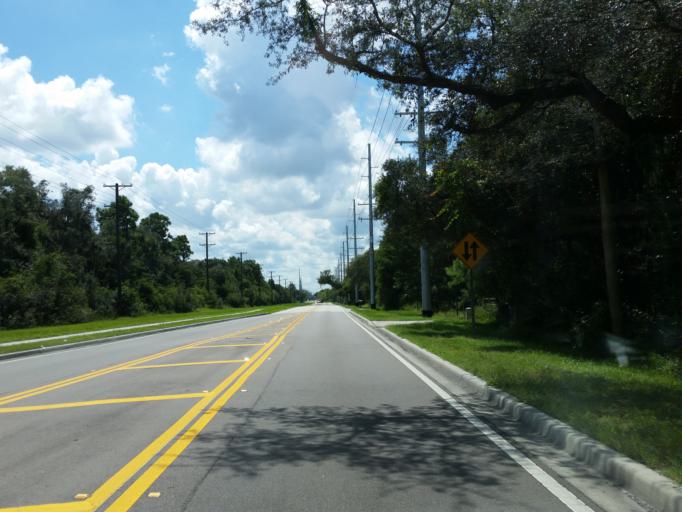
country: US
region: Florida
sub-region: Hillsborough County
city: Riverview
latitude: 27.8508
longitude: -82.3020
